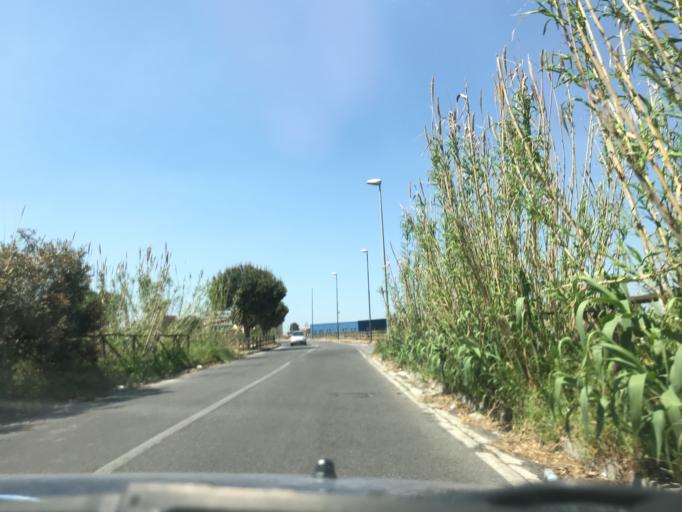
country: IT
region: Campania
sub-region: Provincia di Napoli
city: Villaricca
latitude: 40.9154
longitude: 14.1799
